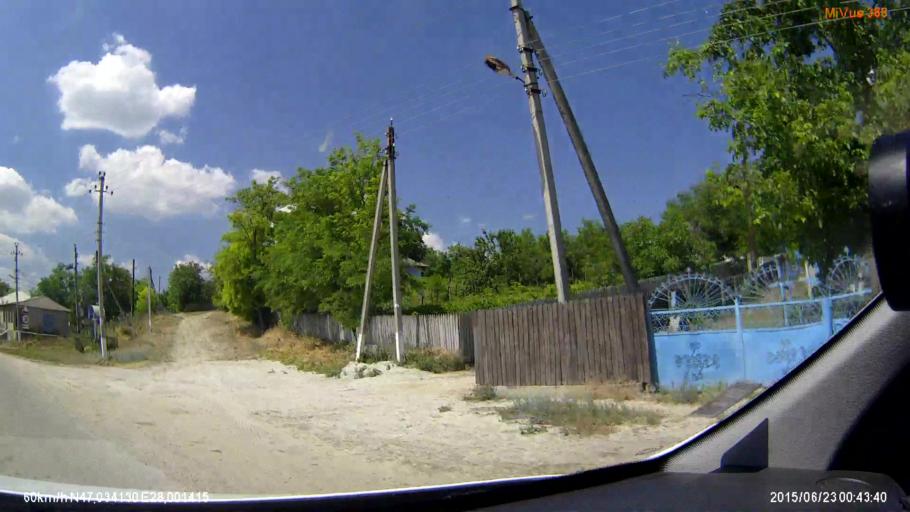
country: RO
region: Iasi
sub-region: Comuna Grozesti
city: Grozesti
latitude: 47.0341
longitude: 28.0016
